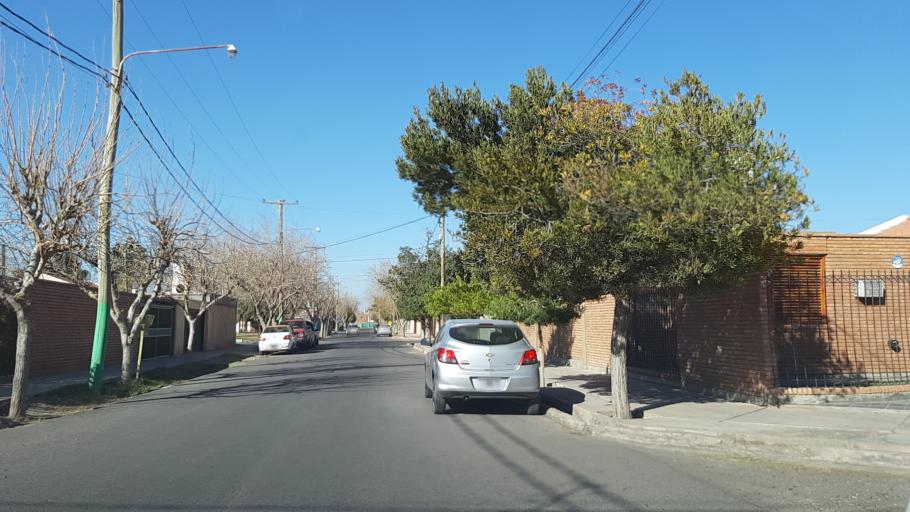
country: AR
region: San Juan
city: Villa Paula de Sarmiento
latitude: -31.5164
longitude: -68.5898
